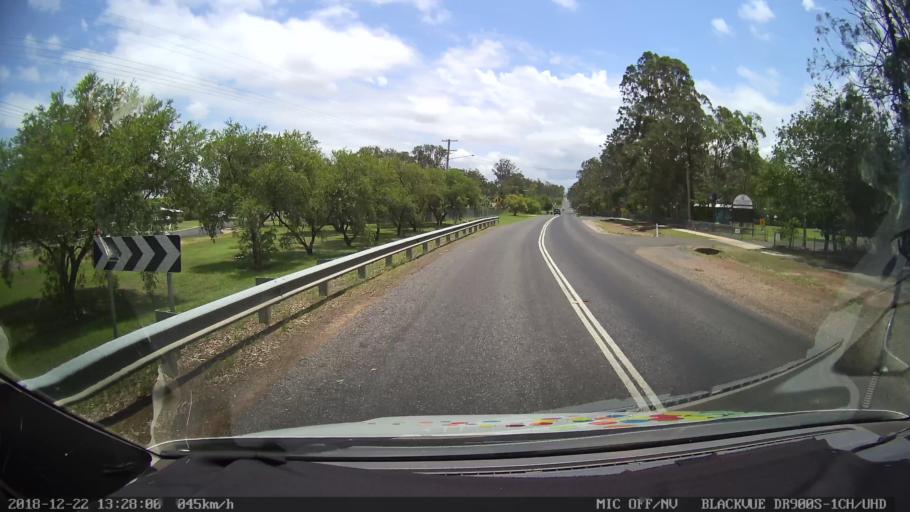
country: AU
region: New South Wales
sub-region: Clarence Valley
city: Coutts Crossing
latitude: -29.8314
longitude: 152.8910
